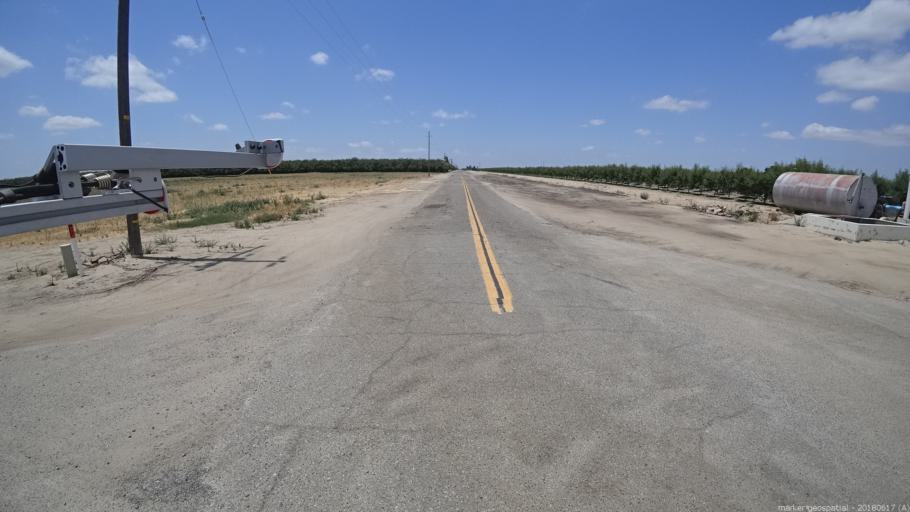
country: US
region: California
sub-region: Fresno County
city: Biola
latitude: 36.8222
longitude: -120.1330
